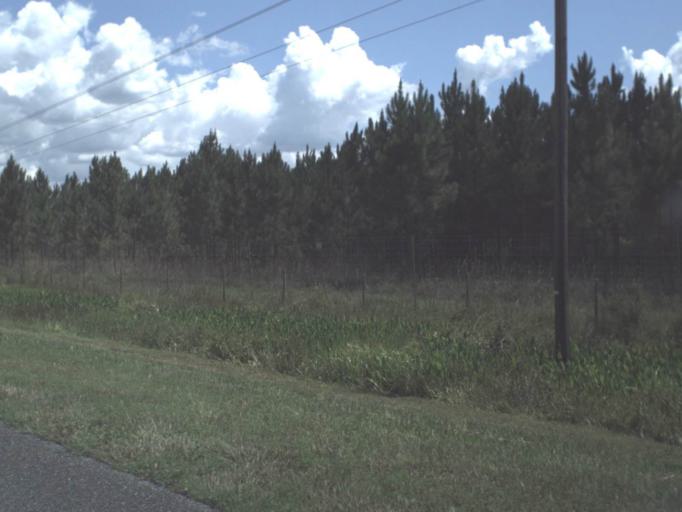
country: US
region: Florida
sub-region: Taylor County
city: Steinhatchee
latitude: 29.8449
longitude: -83.3747
